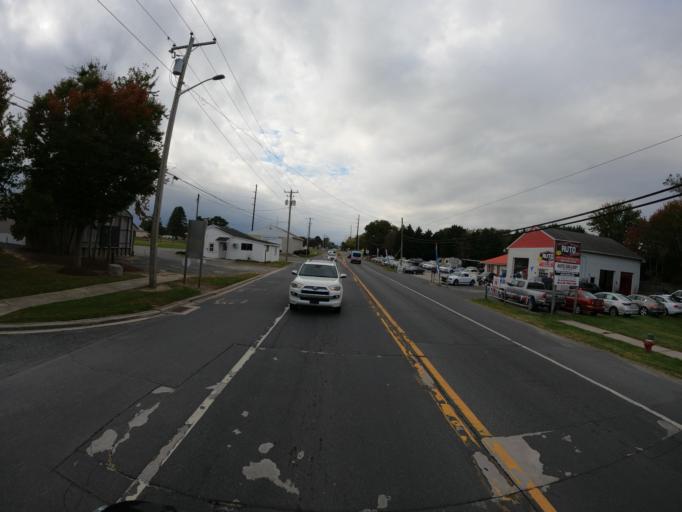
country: US
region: Delaware
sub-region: Sussex County
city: Lewes
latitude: 38.7645
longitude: -75.1496
